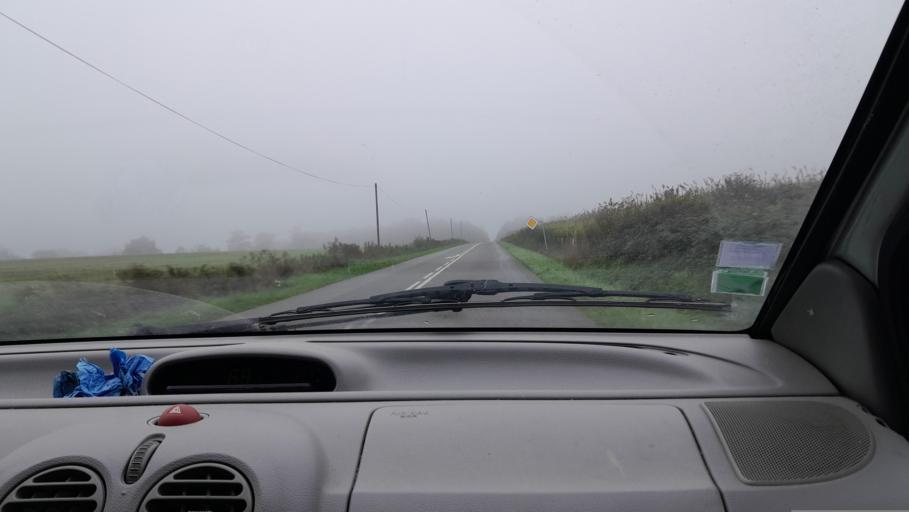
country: FR
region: Pays de la Loire
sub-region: Departement de la Mayenne
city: Loiron
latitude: 48.0178
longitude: -0.9359
